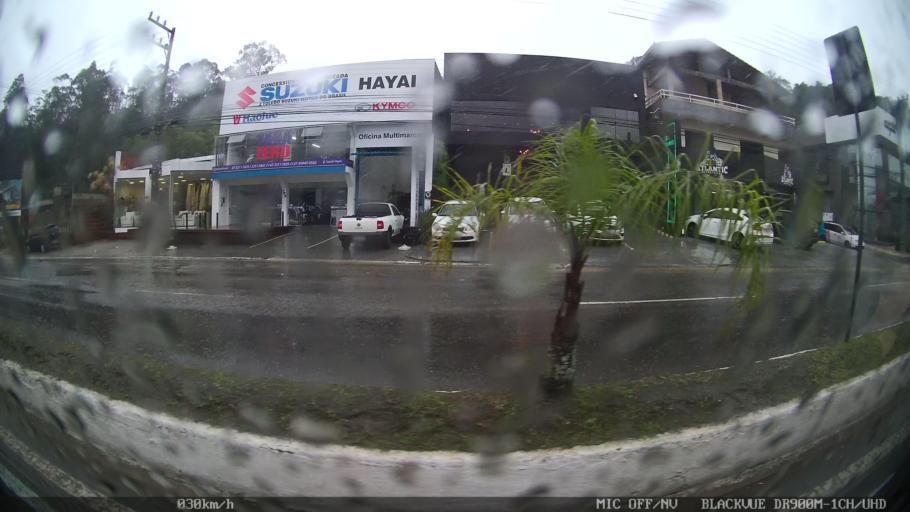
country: BR
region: Santa Catarina
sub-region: Balneario Camboriu
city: Balneario Camboriu
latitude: -26.9634
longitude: -48.6395
